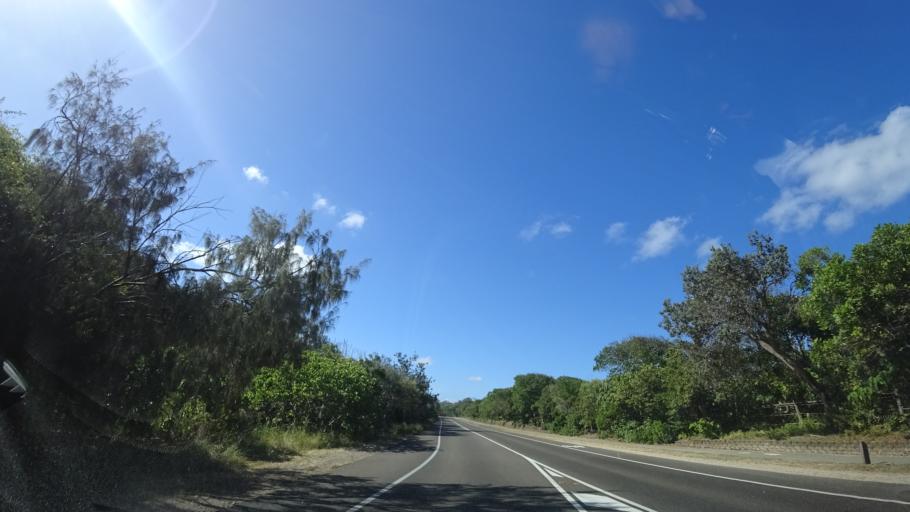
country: AU
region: Queensland
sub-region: Sunshine Coast
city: Mooloolaba
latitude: -26.6085
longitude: 153.0989
